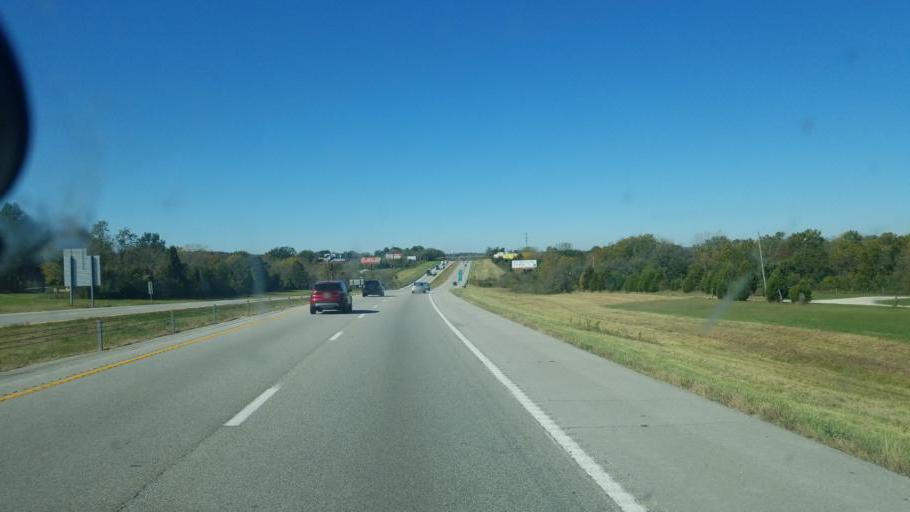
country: US
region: Missouri
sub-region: Jackson County
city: Oak Grove
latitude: 39.0171
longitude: -94.1570
